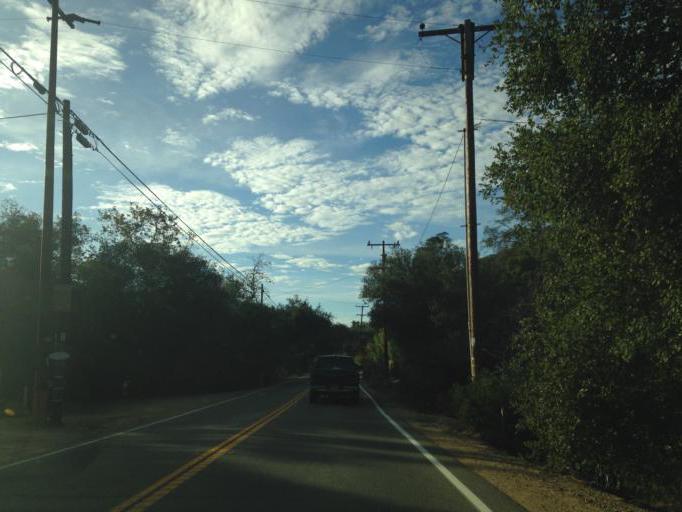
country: US
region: California
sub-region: San Diego County
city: Rainbow
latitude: 33.4171
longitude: -117.0871
